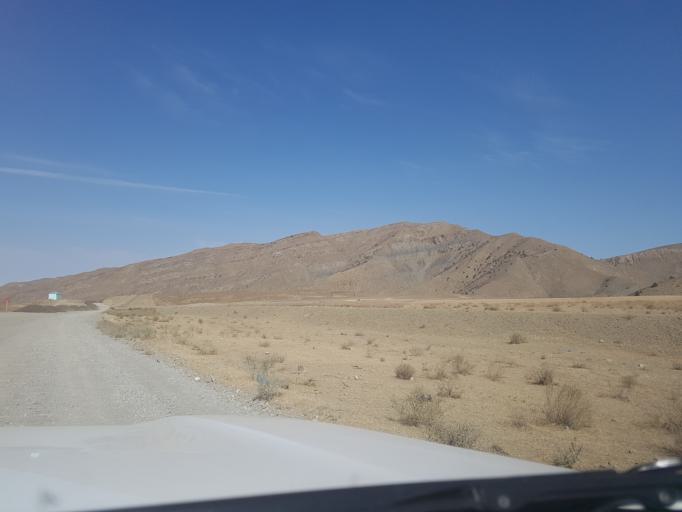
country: TM
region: Ahal
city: Baharly
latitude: 38.4408
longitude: 57.0415
